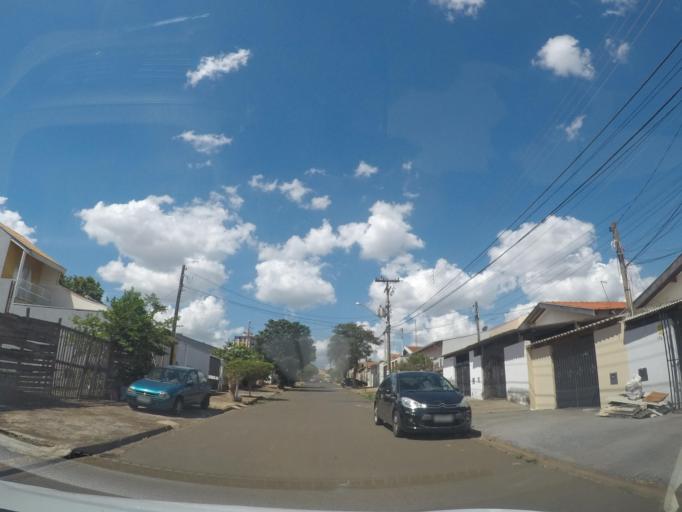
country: BR
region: Sao Paulo
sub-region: Sumare
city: Sumare
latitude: -22.8345
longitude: -47.2767
